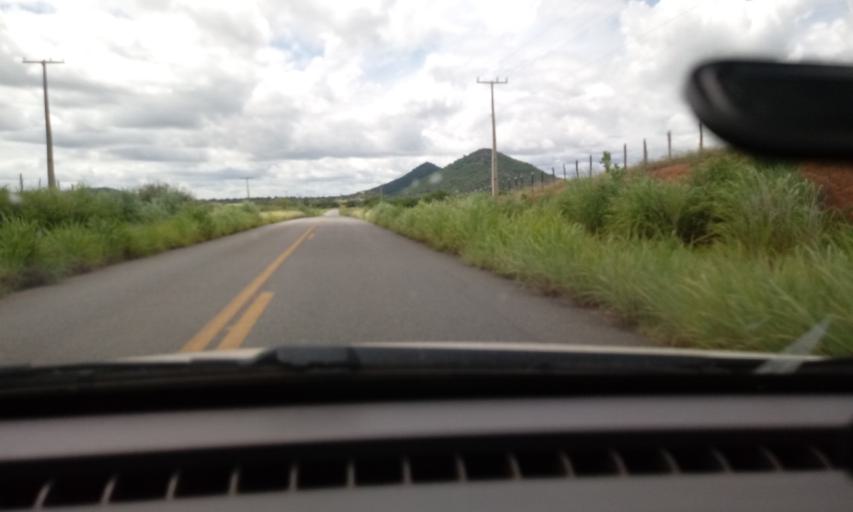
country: BR
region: Bahia
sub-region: Guanambi
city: Guanambi
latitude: -14.0794
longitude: -42.8779
